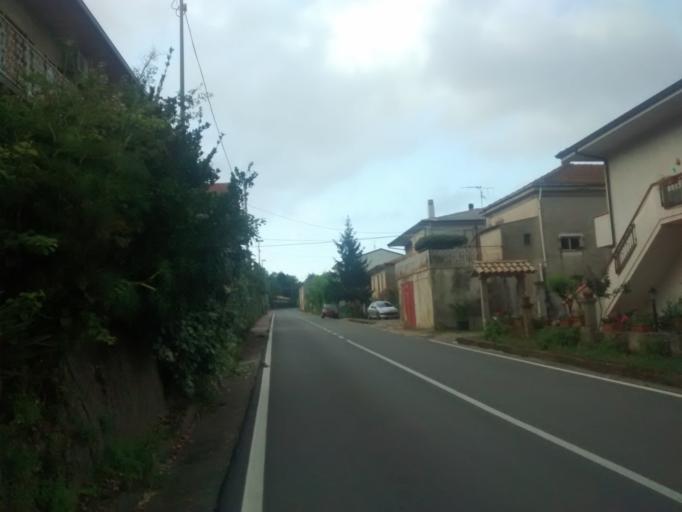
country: IT
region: Calabria
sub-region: Provincia di Catanzaro
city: Cortale
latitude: 38.8915
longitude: 16.4057
